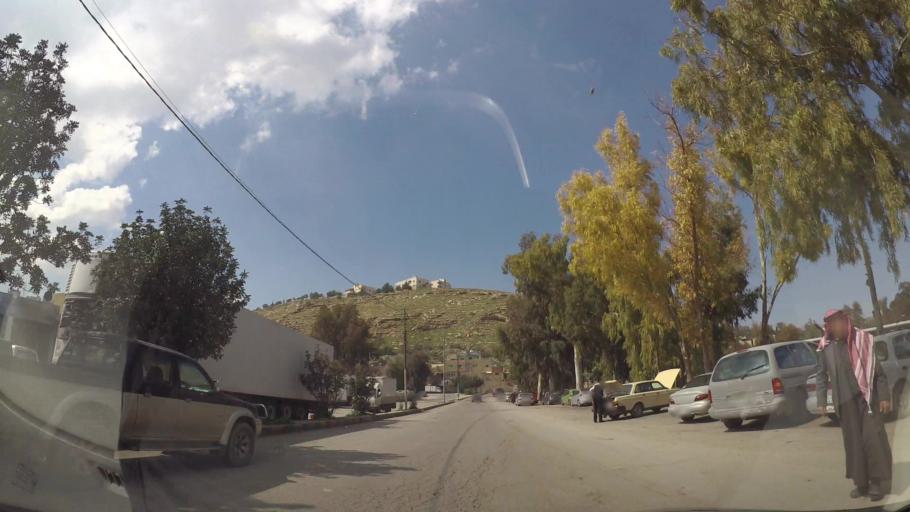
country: JO
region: Amman
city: Amman
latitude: 31.9815
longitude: 35.9763
